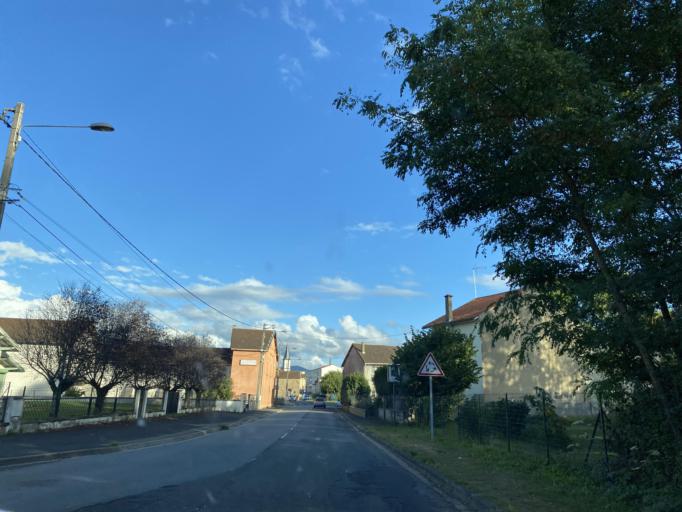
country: FR
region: Auvergne
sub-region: Departement du Puy-de-Dome
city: Puy-Guillaume
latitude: 45.9616
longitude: 3.4671
